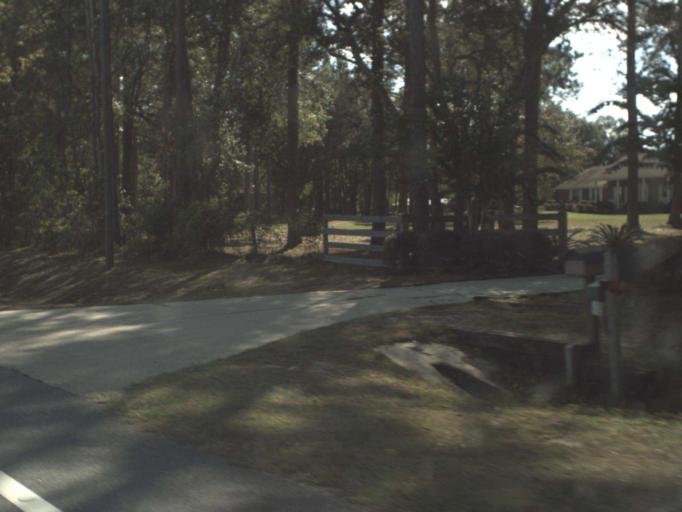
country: US
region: Florida
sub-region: Jefferson County
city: Monticello
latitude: 30.4596
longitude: -84.0191
